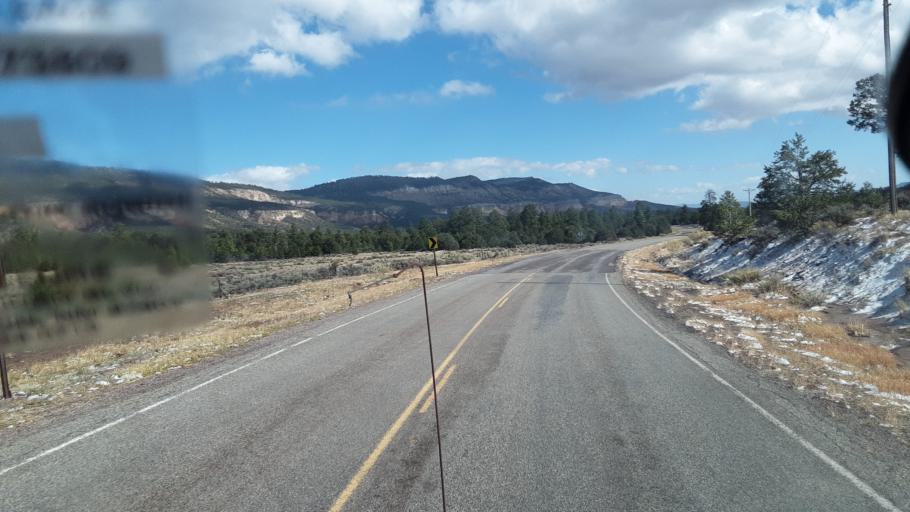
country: US
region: New Mexico
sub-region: Rio Arriba County
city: Santa Teresa
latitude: 36.2005
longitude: -106.7357
